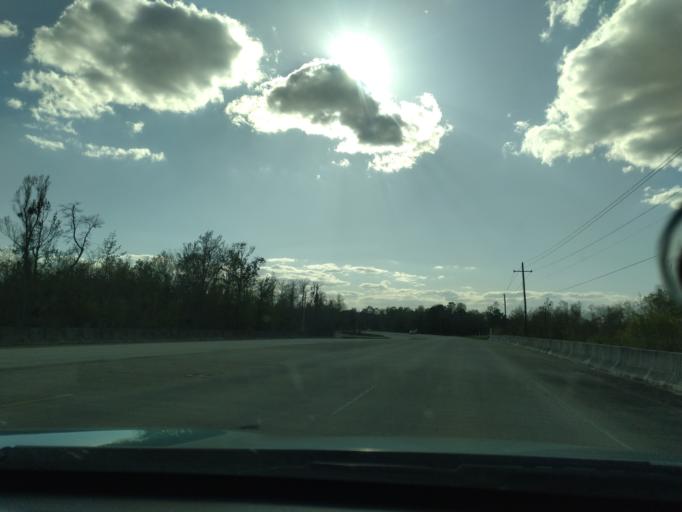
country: US
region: South Carolina
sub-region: Williamsburg County
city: Kingstree
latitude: 33.6578
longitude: -79.8715
